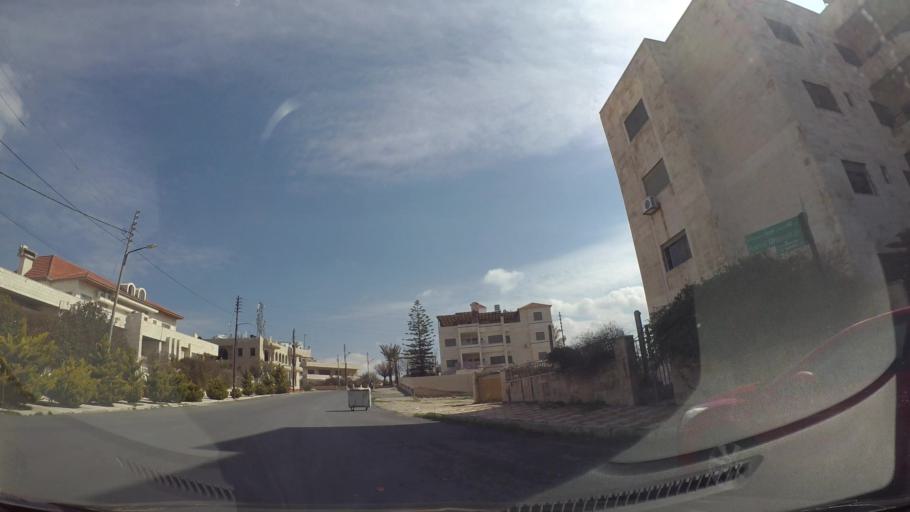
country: JO
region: Amman
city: Al Jubayhah
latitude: 31.9923
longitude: 35.8955
